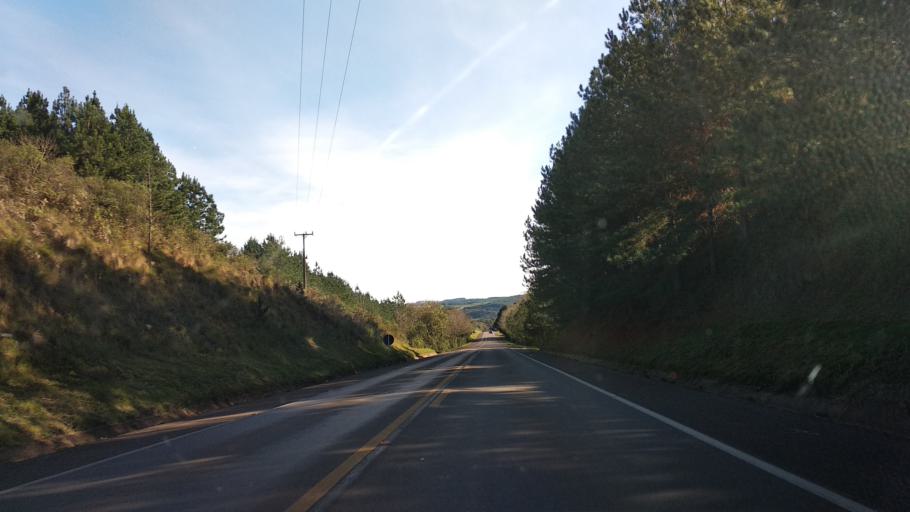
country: BR
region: Santa Catarina
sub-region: Celso Ramos
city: Celso Ramos
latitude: -27.5447
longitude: -51.4255
